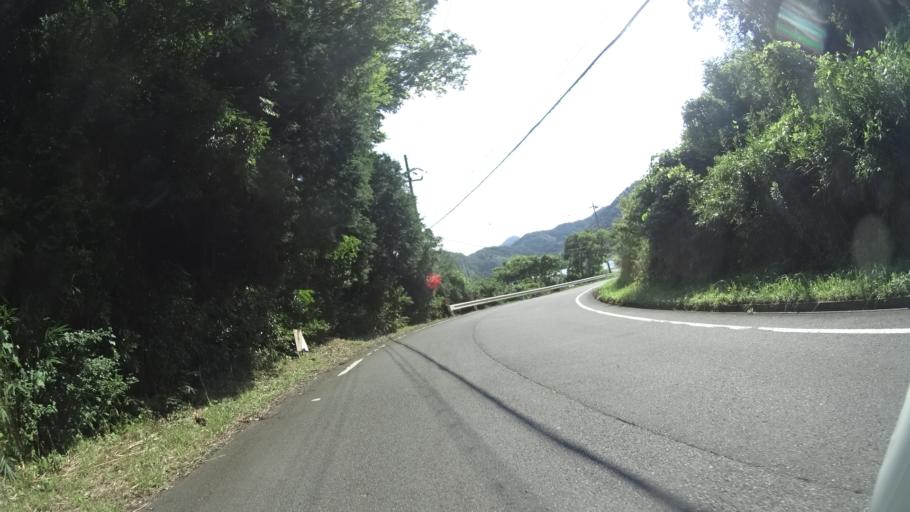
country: JP
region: Kyoto
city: Maizuru
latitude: 35.4819
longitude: 135.3221
